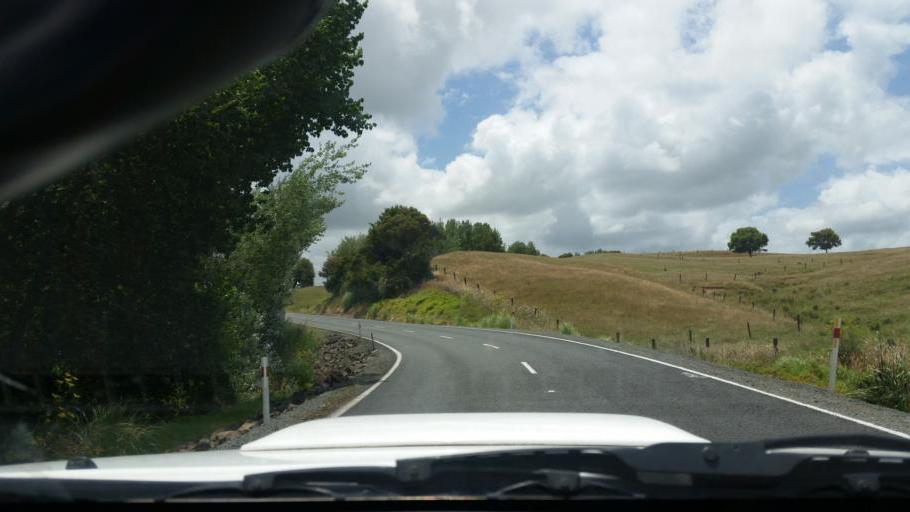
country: NZ
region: Auckland
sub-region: Auckland
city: Wellsford
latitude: -36.1281
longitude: 174.3278
